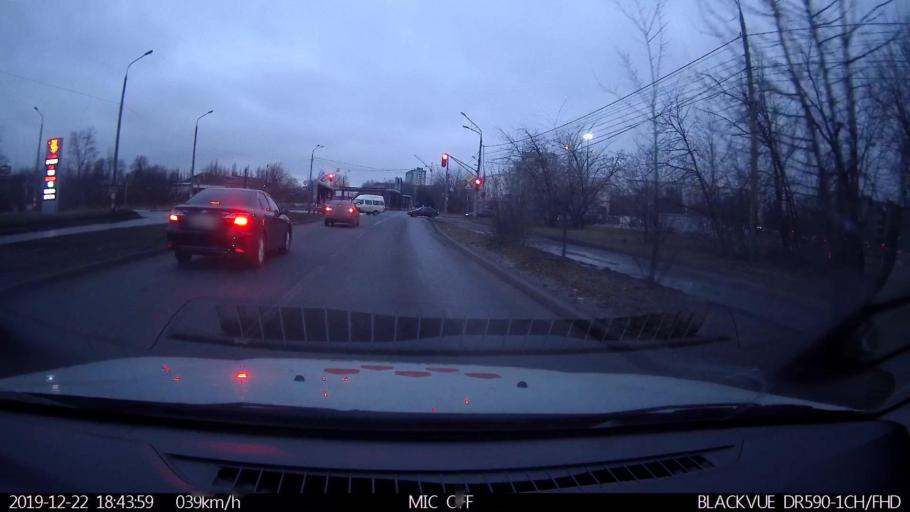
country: RU
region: Nizjnij Novgorod
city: Nizhniy Novgorod
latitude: 56.3384
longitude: 43.8875
